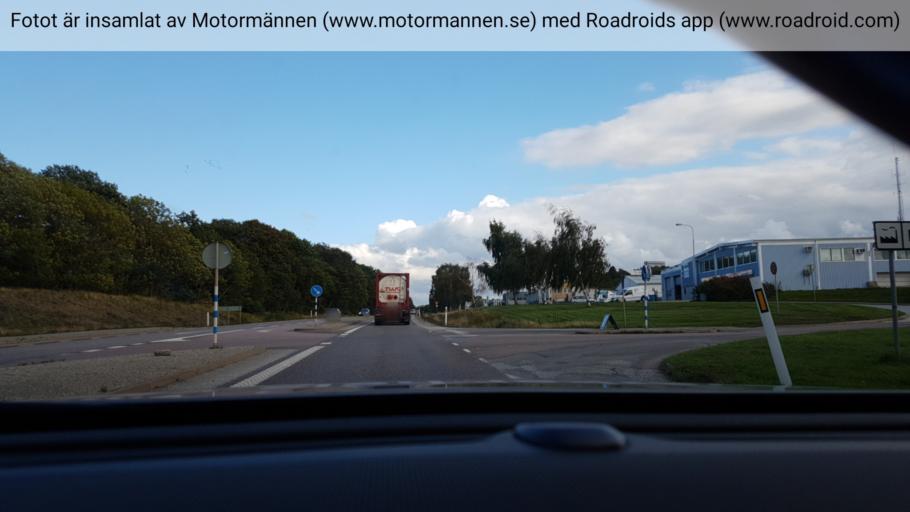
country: SE
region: Vaestra Goetaland
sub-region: Stenungsunds Kommun
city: Stenungsund
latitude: 58.0754
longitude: 11.8397
